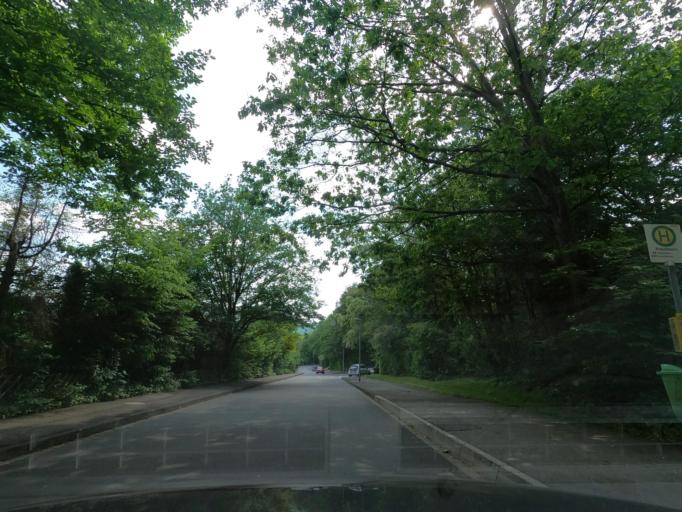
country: DE
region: North Rhine-Westphalia
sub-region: Regierungsbezirk Arnsberg
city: Luedenscheid
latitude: 51.2454
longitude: 7.6107
